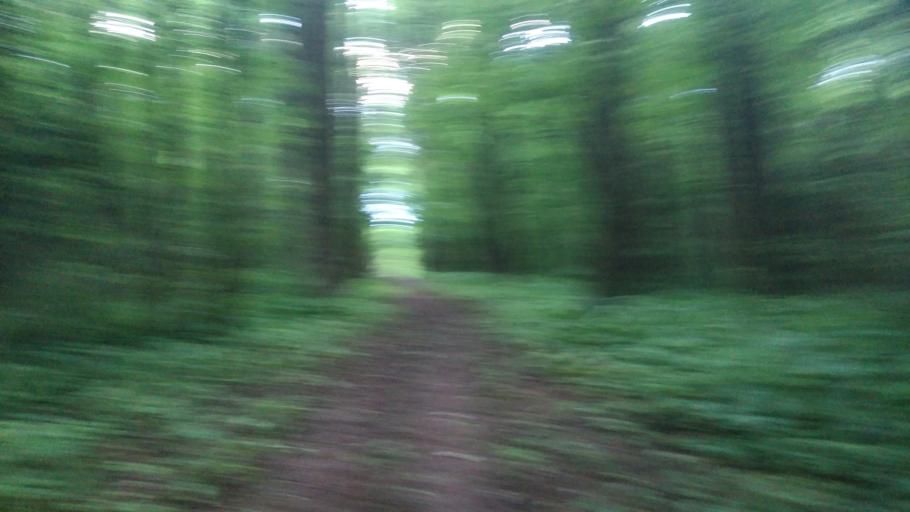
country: RU
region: Perm
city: Ferma
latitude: 57.9635
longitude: 56.3415
